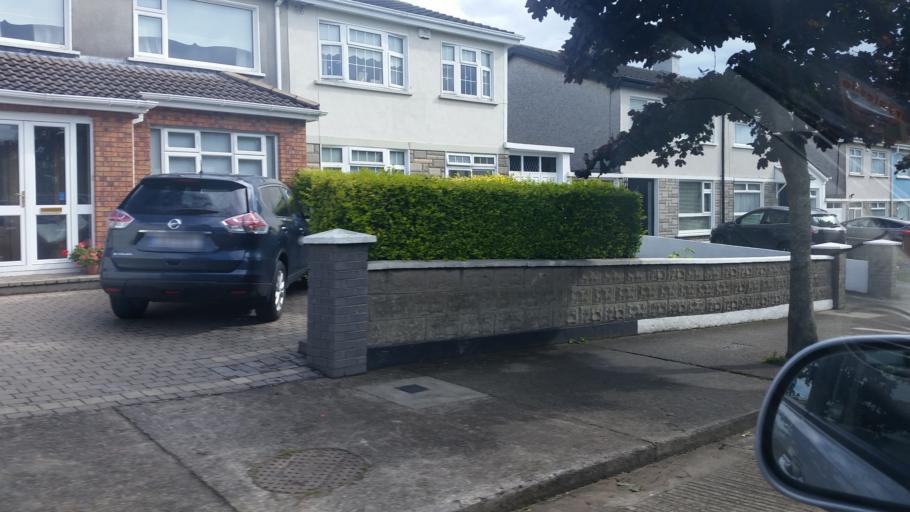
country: IE
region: Leinster
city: Portmarnock
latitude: 53.4335
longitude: -6.1271
